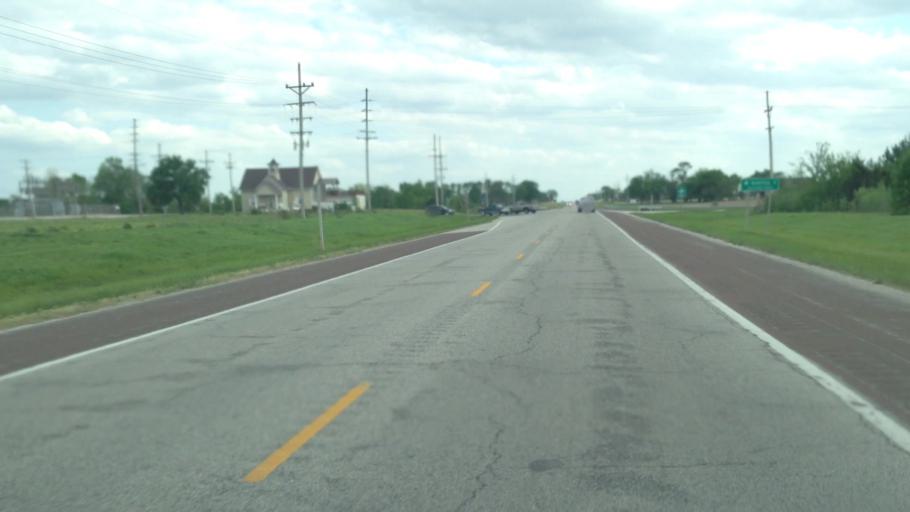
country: US
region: Kansas
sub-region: Franklin County
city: Ottawa
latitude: 38.5516
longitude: -95.2678
